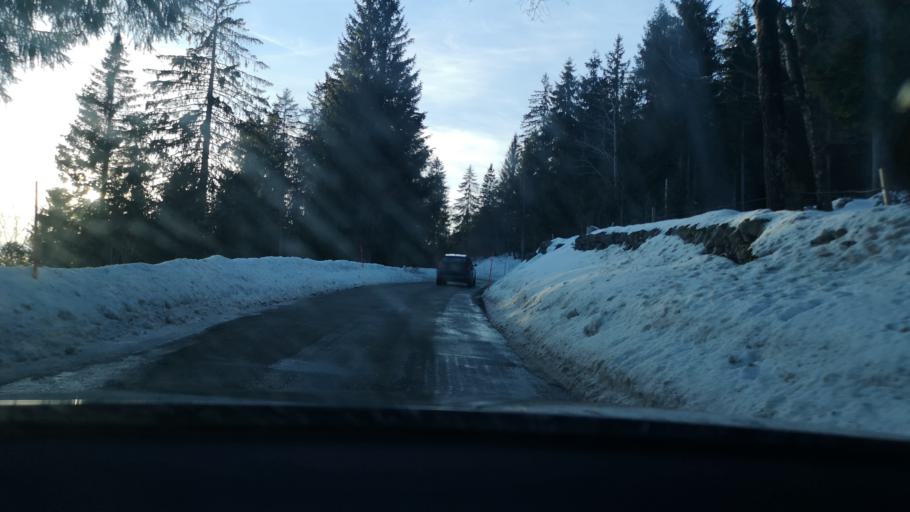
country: FR
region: Franche-Comte
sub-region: Departement du Doubs
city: Montlebon
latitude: 46.9774
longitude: 6.5667
